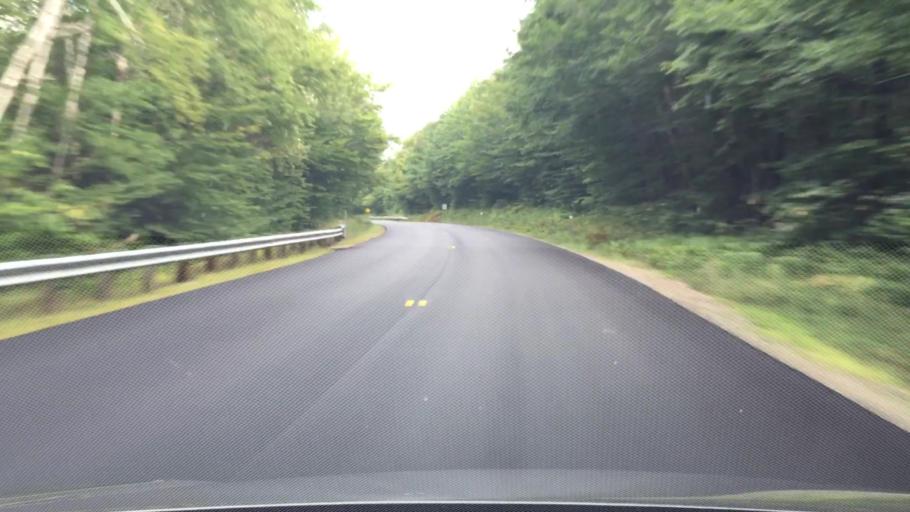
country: US
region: New Hampshire
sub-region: Carroll County
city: Sandwich
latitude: 44.0174
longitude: -71.4332
